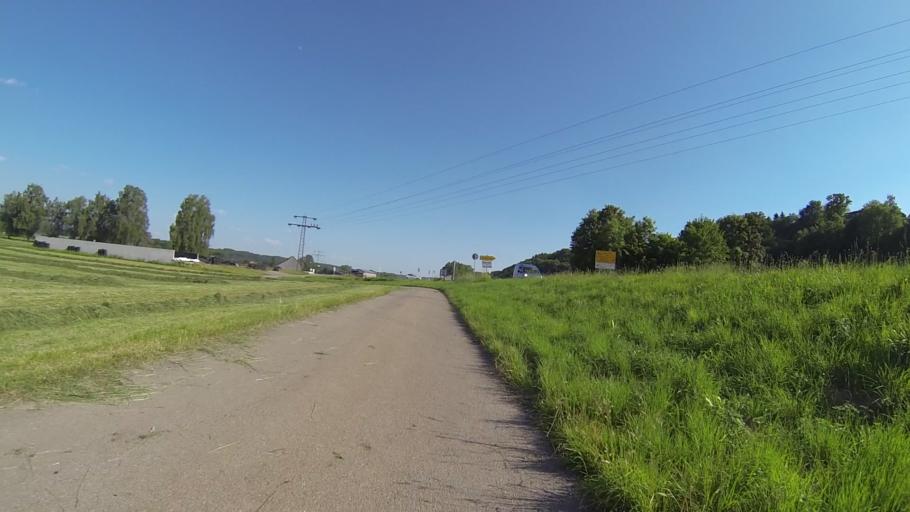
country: DE
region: Baden-Wuerttemberg
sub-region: Tuebingen Region
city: Warthausen
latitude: 48.1522
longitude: 9.7899
